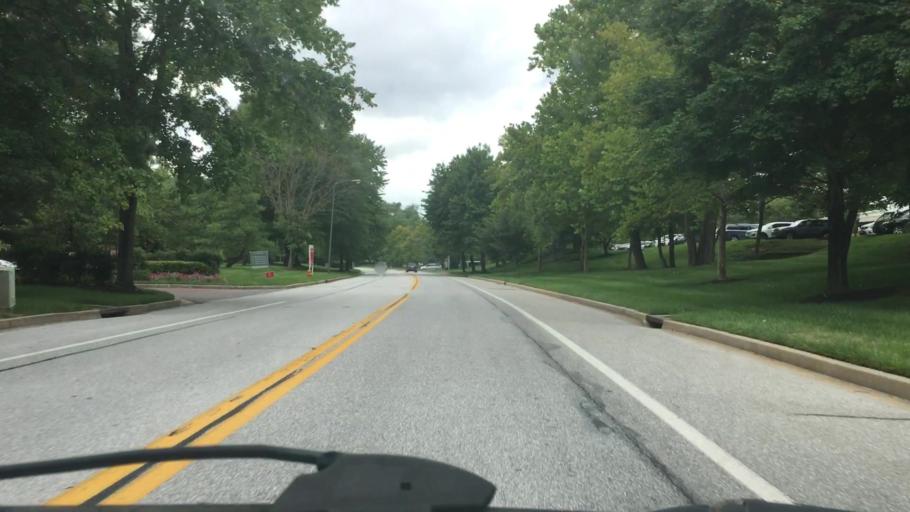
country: US
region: Maryland
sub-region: Howard County
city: Savage
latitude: 39.1677
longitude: -76.8431
